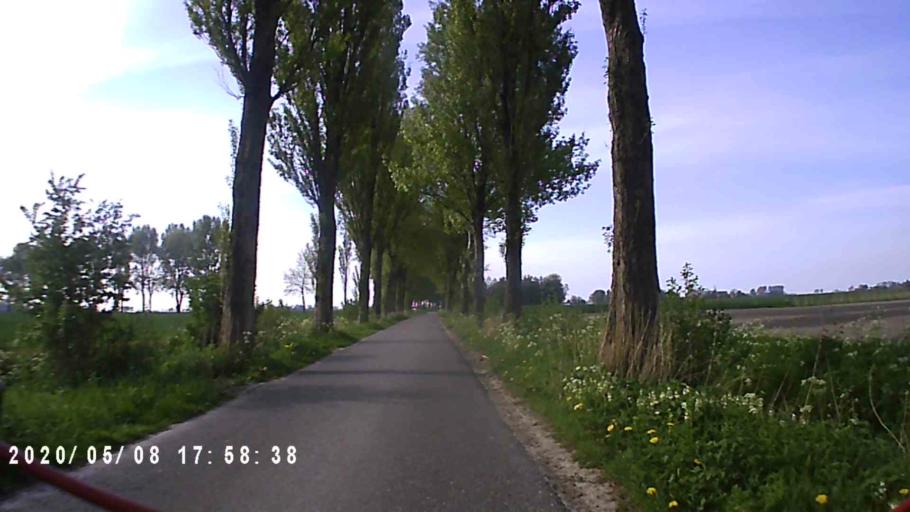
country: NL
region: Groningen
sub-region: Gemeente Winsum
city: Winsum
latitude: 53.3712
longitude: 6.4831
